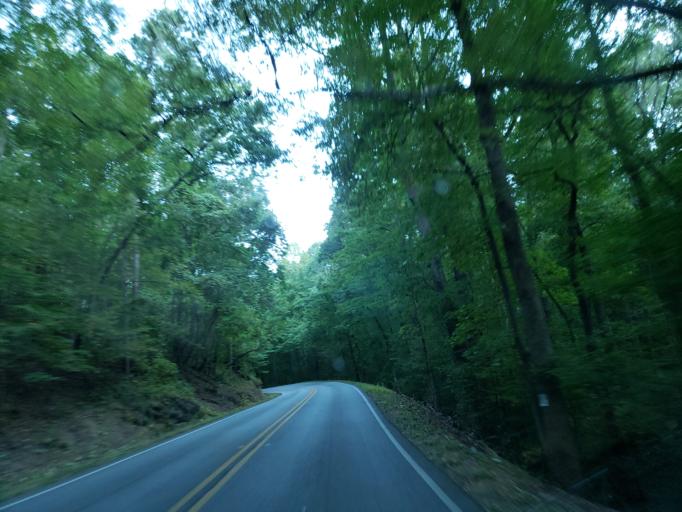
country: US
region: Georgia
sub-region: Bartow County
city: Rydal
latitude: 34.3613
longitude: -84.5795
